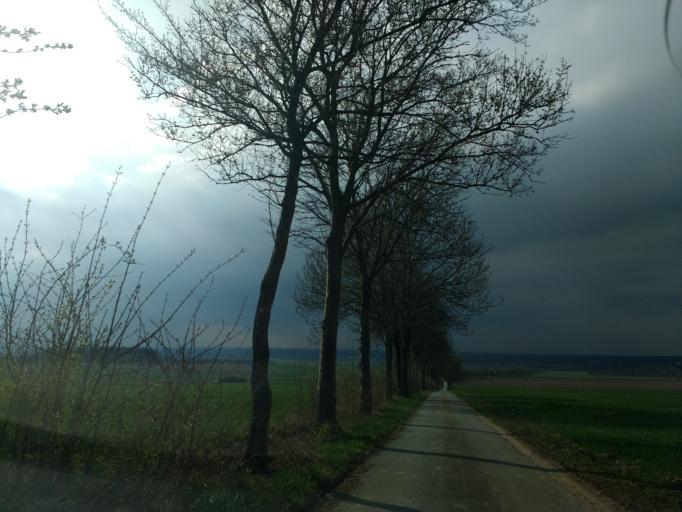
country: DE
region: North Rhine-Westphalia
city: Bad Lippspringe
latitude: 51.7580
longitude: 8.8623
